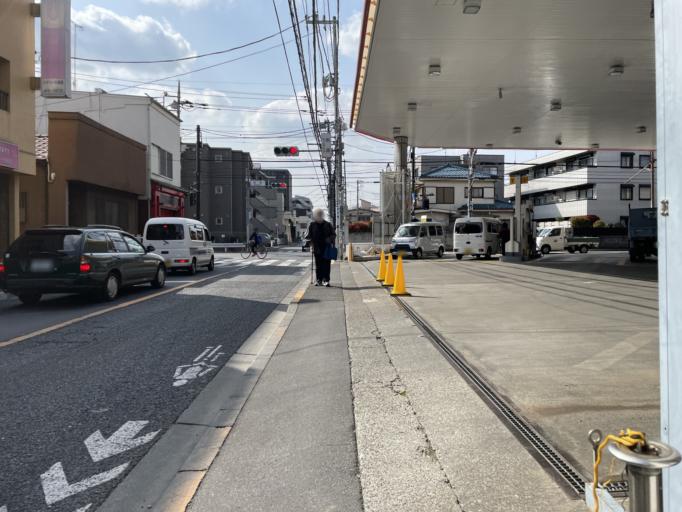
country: JP
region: Tokyo
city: Mitaka-shi
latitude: 35.6920
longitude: 139.5651
